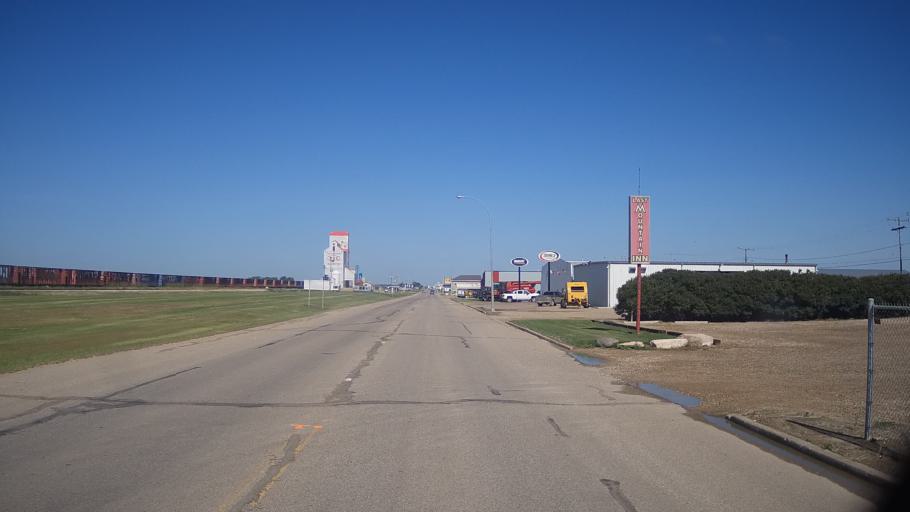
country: CA
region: Saskatchewan
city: Watrous
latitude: 51.6663
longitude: -105.4529
